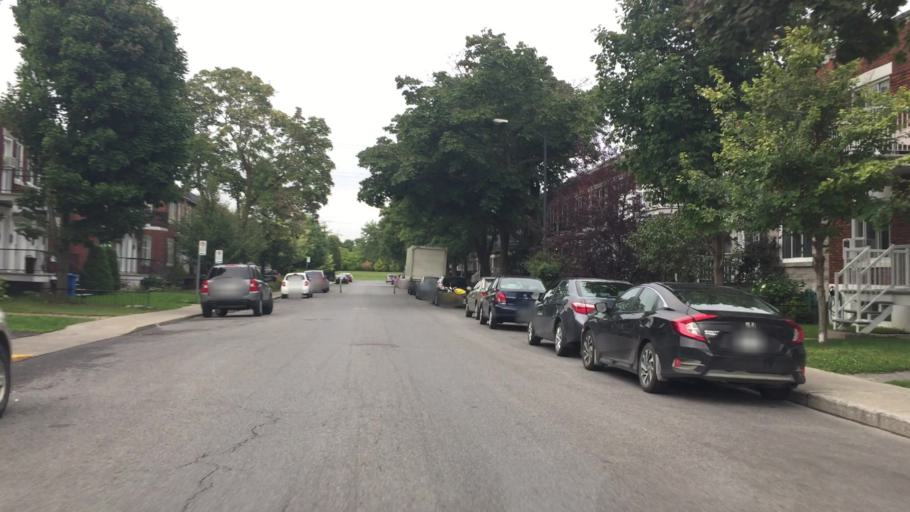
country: CA
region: Quebec
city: Saint-Raymond
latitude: 45.4465
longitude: -73.5867
